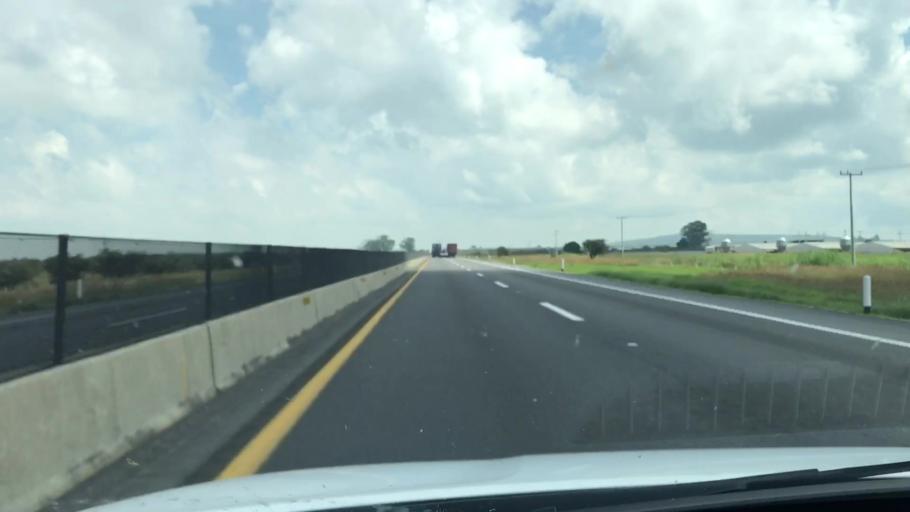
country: MX
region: Jalisco
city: Valle de Guadalupe
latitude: 21.0085
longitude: -102.5790
